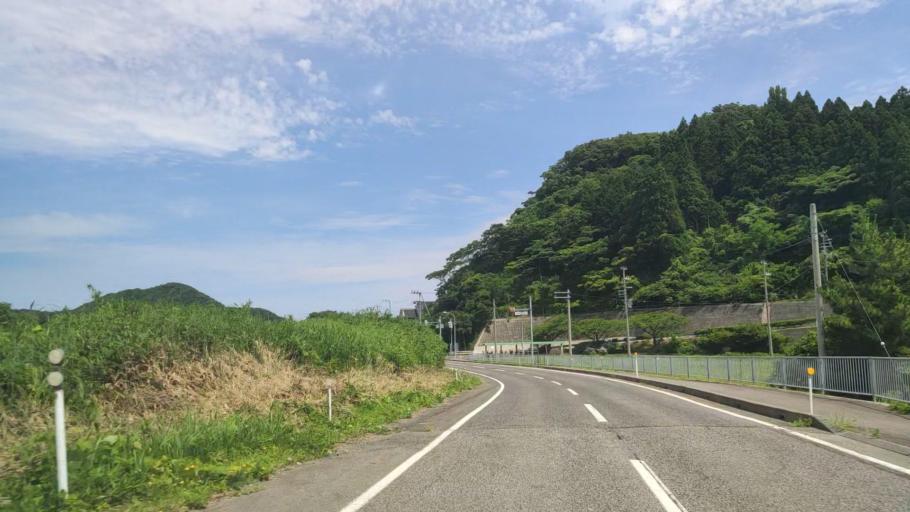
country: JP
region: Hyogo
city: Toyooka
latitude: 35.6512
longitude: 134.7636
